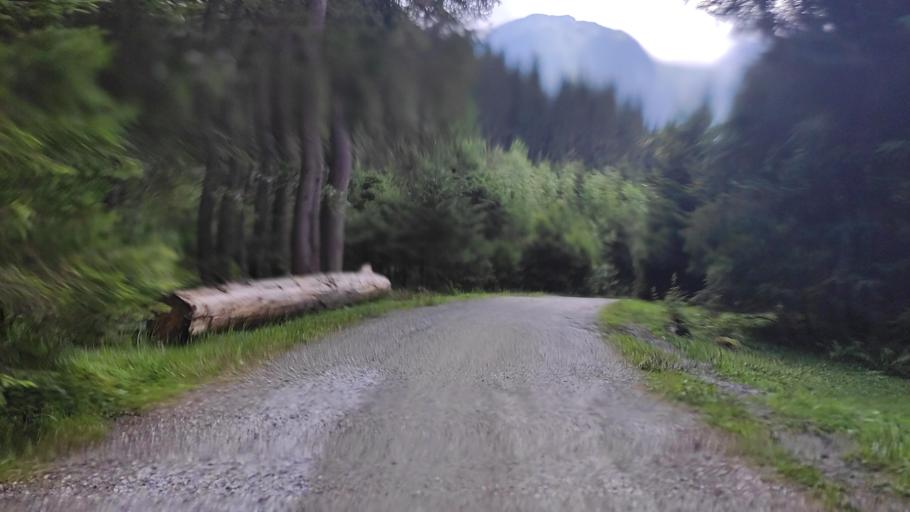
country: AT
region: Salzburg
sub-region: Politischer Bezirk Zell am See
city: Krimml
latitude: 47.2197
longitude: 12.1823
